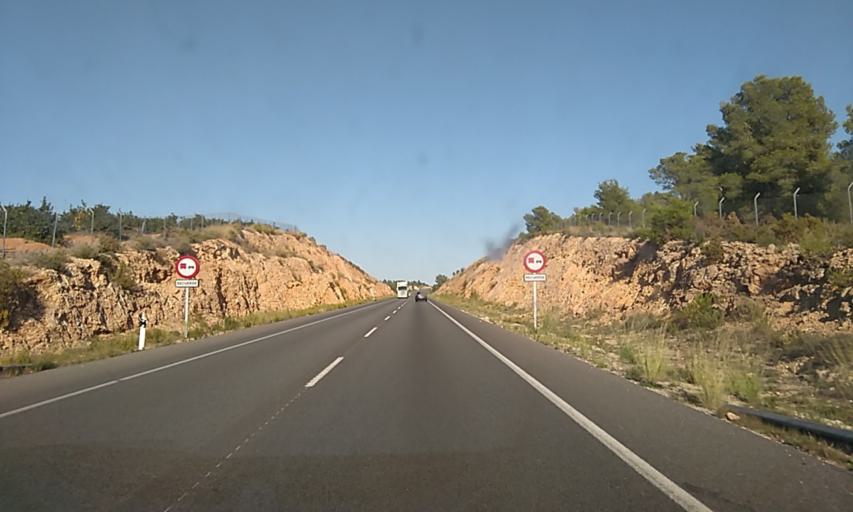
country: ES
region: Valencia
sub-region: Provincia de Castello
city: Torreblanca
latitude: 40.2145
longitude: 0.1512
